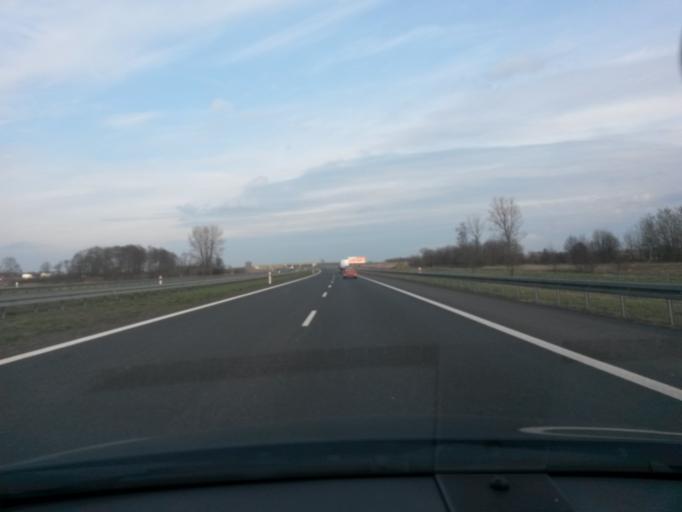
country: PL
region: Lodz Voivodeship
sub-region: Powiat zgierski
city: Parzeczew
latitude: 51.9421
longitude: 19.1873
